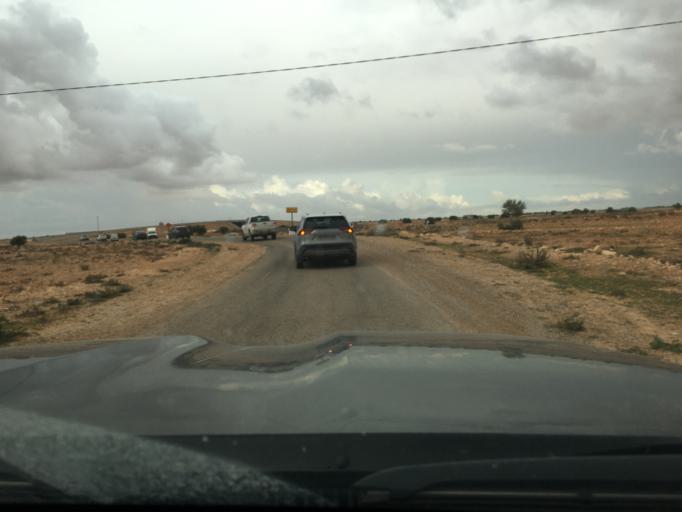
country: TN
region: Madanin
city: Medenine
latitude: 33.2955
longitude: 10.6092
